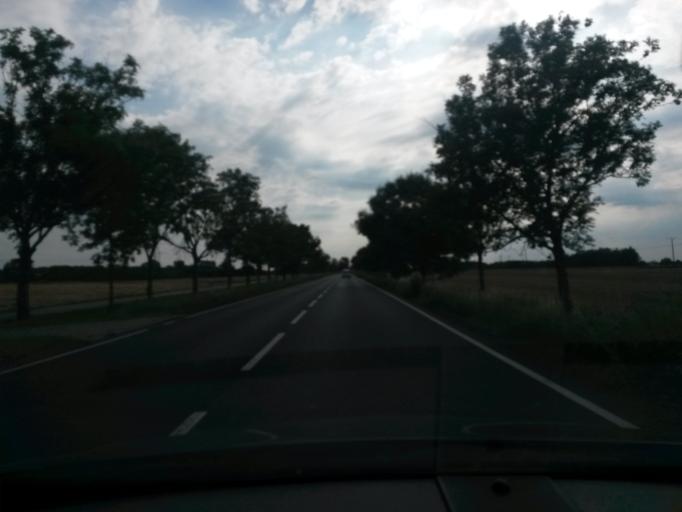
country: PL
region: Greater Poland Voivodeship
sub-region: Powiat rawicki
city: Rawicz
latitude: 51.6258
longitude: 16.8892
